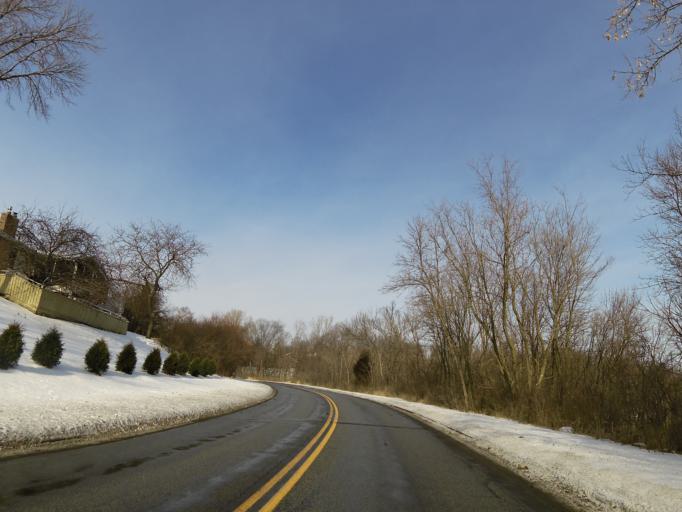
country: US
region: Minnesota
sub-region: Hennepin County
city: Eden Prairie
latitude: 44.8402
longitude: -93.4099
